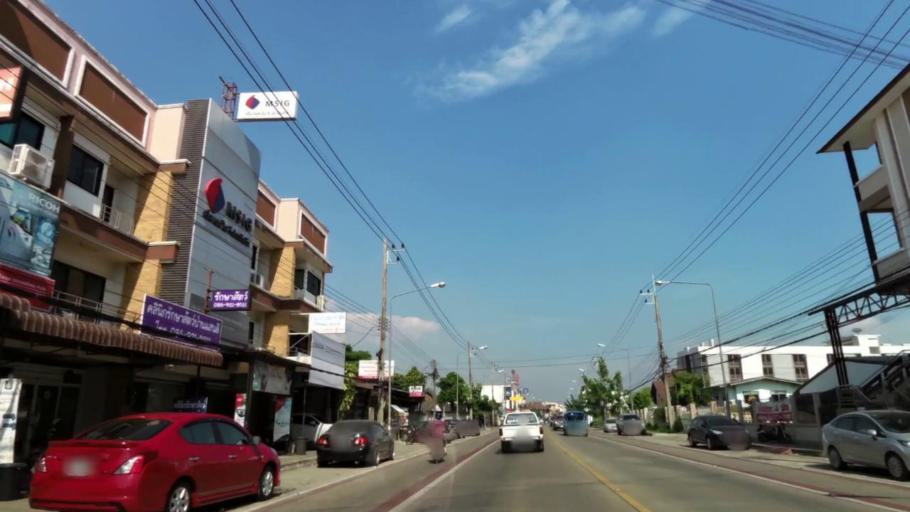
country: TH
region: Chiang Rai
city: Chiang Rai
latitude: 19.9233
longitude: 99.8346
